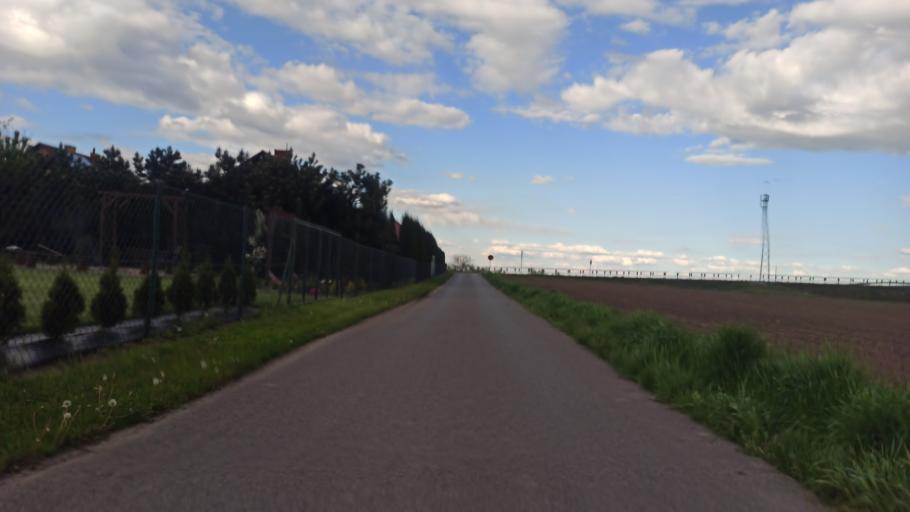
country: PL
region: Subcarpathian Voivodeship
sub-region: Powiat jaroslawski
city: Sosnica
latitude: 49.9162
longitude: 22.8584
